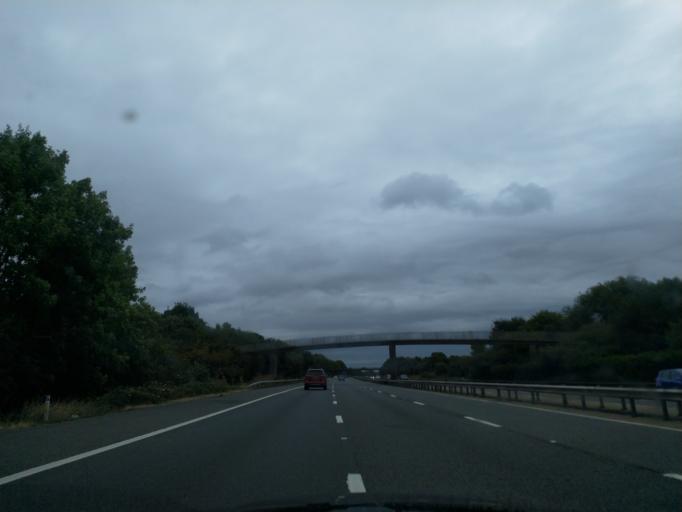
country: GB
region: England
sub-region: Surrey
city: Shepperton
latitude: 51.4026
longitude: -0.4487
